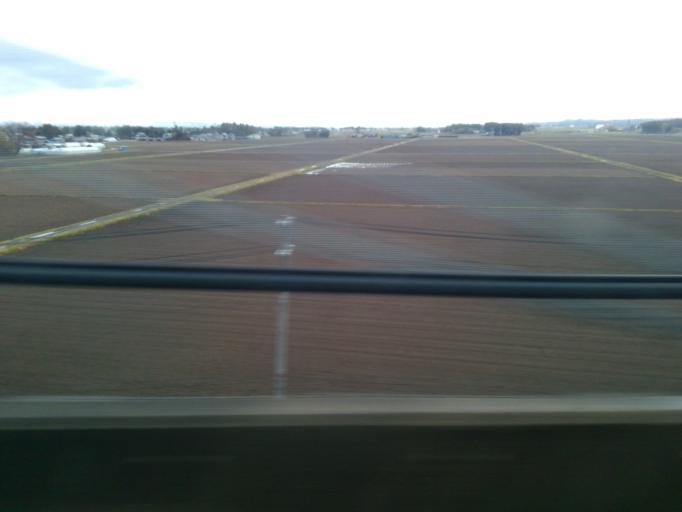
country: JP
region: Miyagi
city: Furukawa
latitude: 38.5521
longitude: 140.9629
